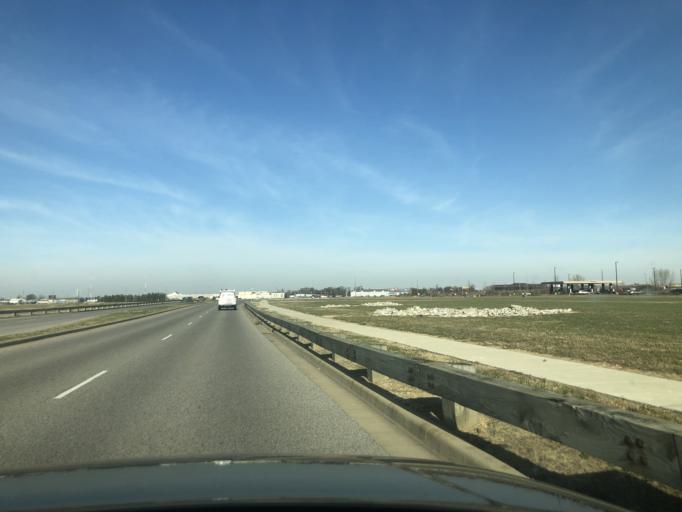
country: US
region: Indiana
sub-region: Vanderburgh County
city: Melody Hill
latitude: 37.9857
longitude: -87.4638
